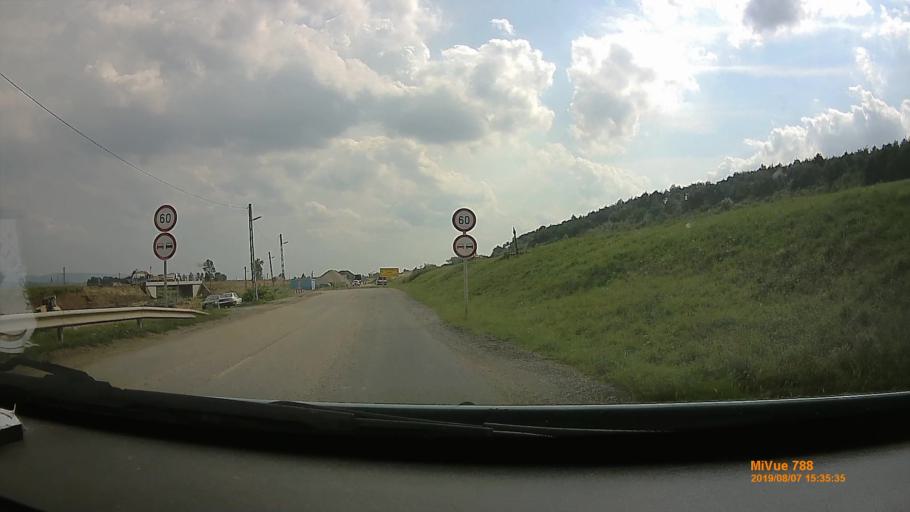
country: HU
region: Borsod-Abauj-Zemplen
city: Encs
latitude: 48.4109
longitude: 21.1732
